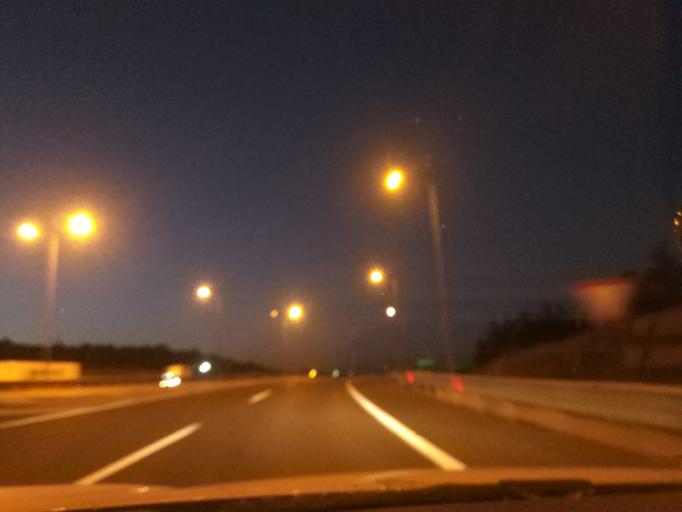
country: TR
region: Istanbul
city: Sancaktepe
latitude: 41.0482
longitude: 29.2766
